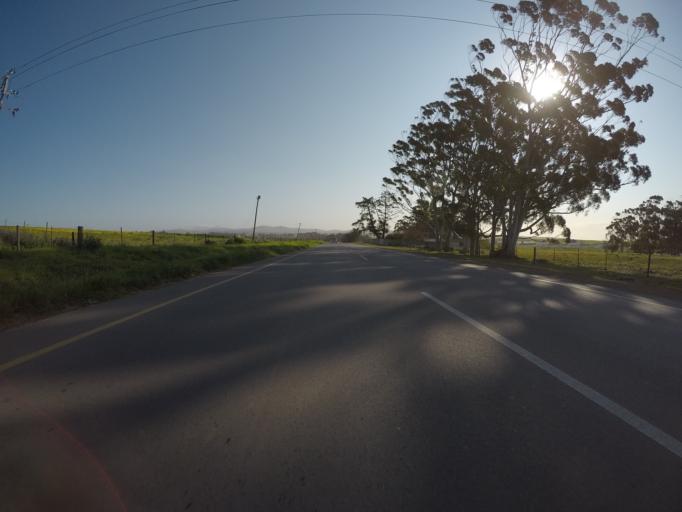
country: ZA
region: Western Cape
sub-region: City of Cape Town
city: Kraaifontein
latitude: -33.7770
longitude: 18.7326
